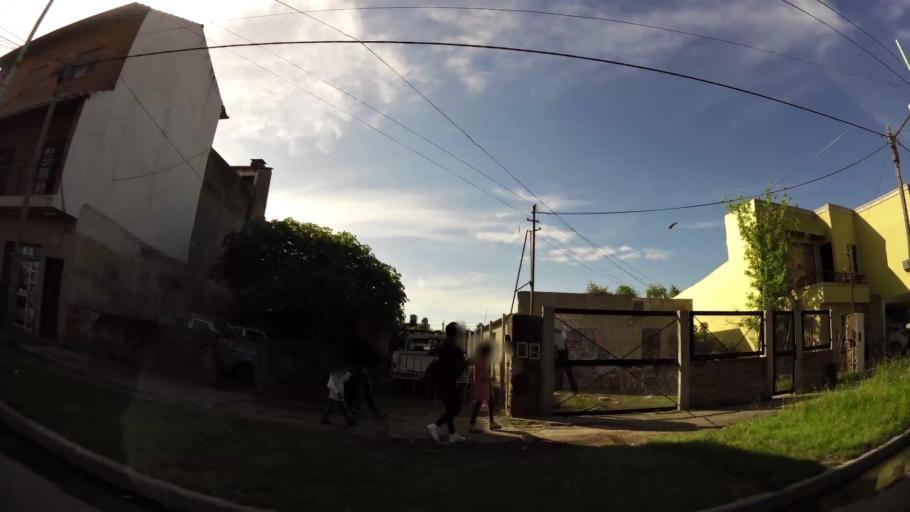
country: AR
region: Buenos Aires
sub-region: Partido de Quilmes
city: Quilmes
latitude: -34.7941
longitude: -58.2351
